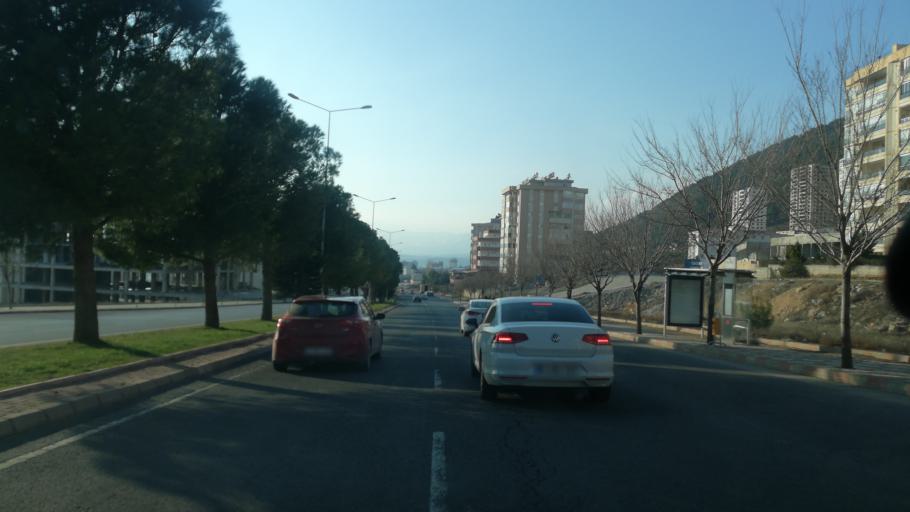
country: TR
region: Kahramanmaras
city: Kahramanmaras
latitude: 37.5970
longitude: 36.8478
